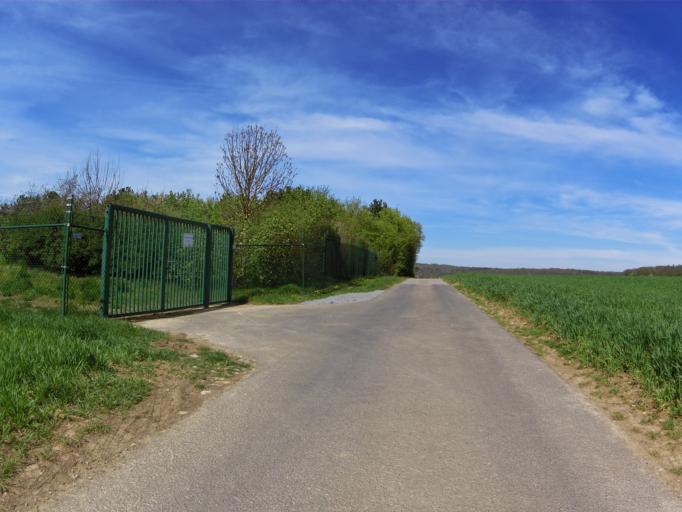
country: DE
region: Bavaria
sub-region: Regierungsbezirk Unterfranken
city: Rimpar
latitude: 49.8600
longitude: 9.9753
